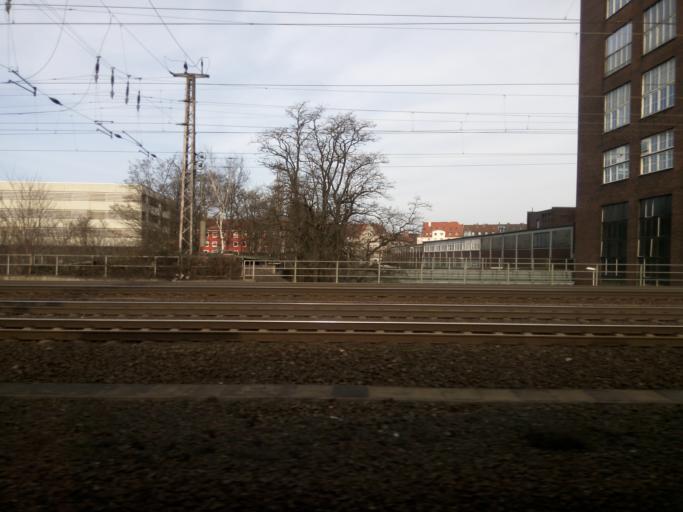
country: DE
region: Lower Saxony
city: Hannover
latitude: 52.3898
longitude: 9.7277
